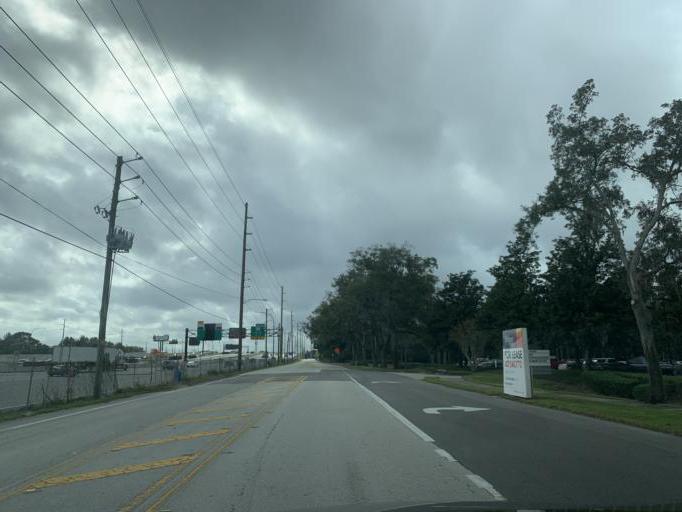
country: US
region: Florida
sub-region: Orange County
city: Eatonville
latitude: 28.6236
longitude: -81.3872
